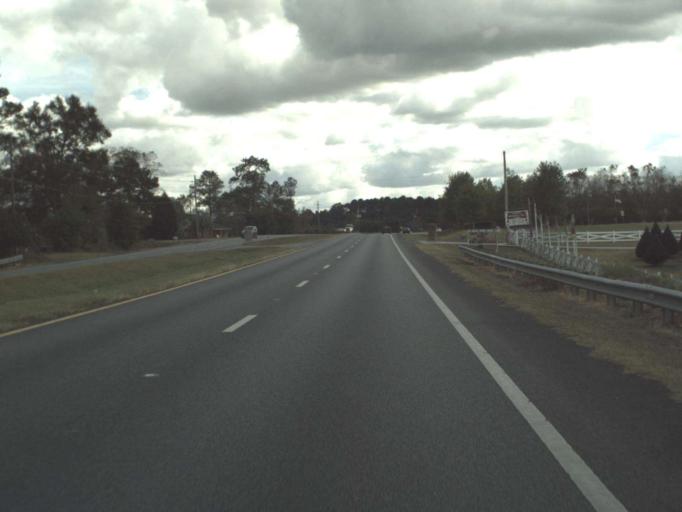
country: US
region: Florida
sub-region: Gadsden County
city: Havana
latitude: 30.5910
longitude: -84.4069
